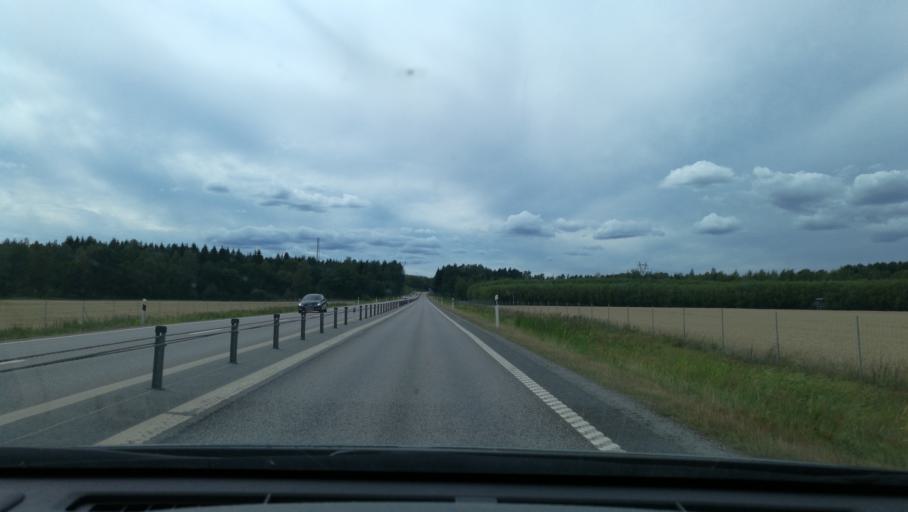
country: SE
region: OEstergoetland
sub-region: Norrkopings Kommun
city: Jursla
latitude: 58.6341
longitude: 16.1190
